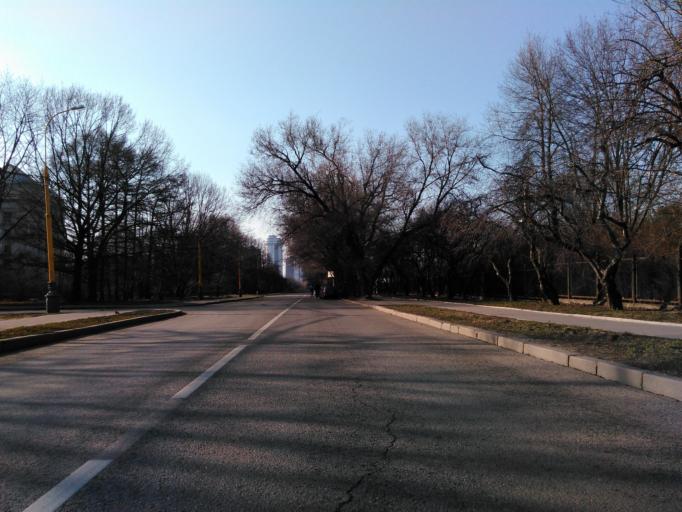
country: RU
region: Moscow
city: Vorob'yovo
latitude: 55.7046
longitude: 37.5250
